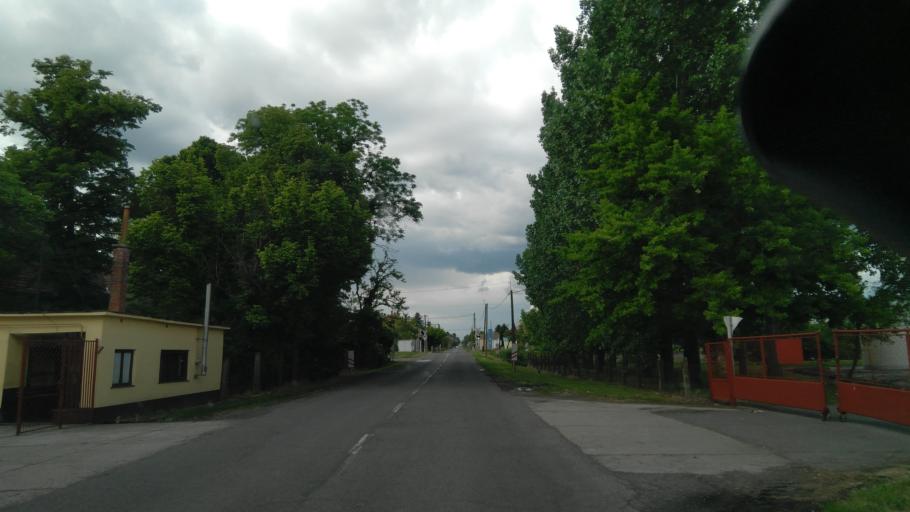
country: HU
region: Bekes
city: Gadoros
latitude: 46.6554
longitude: 20.5901
